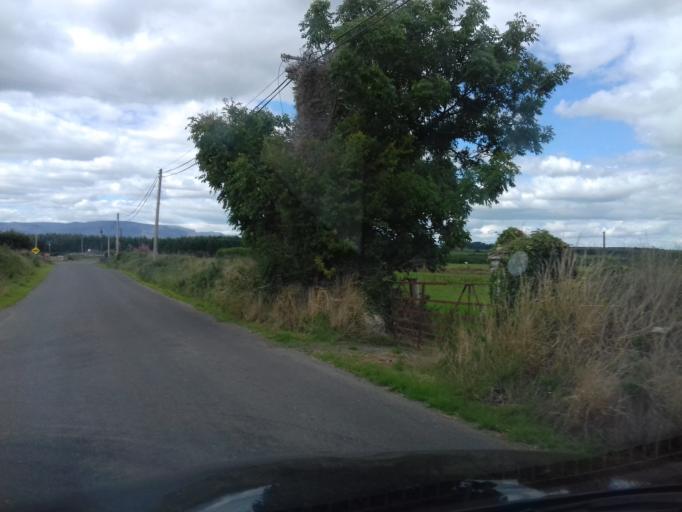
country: IE
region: Munster
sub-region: Waterford
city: Portlaw
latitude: 52.1819
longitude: -7.2981
